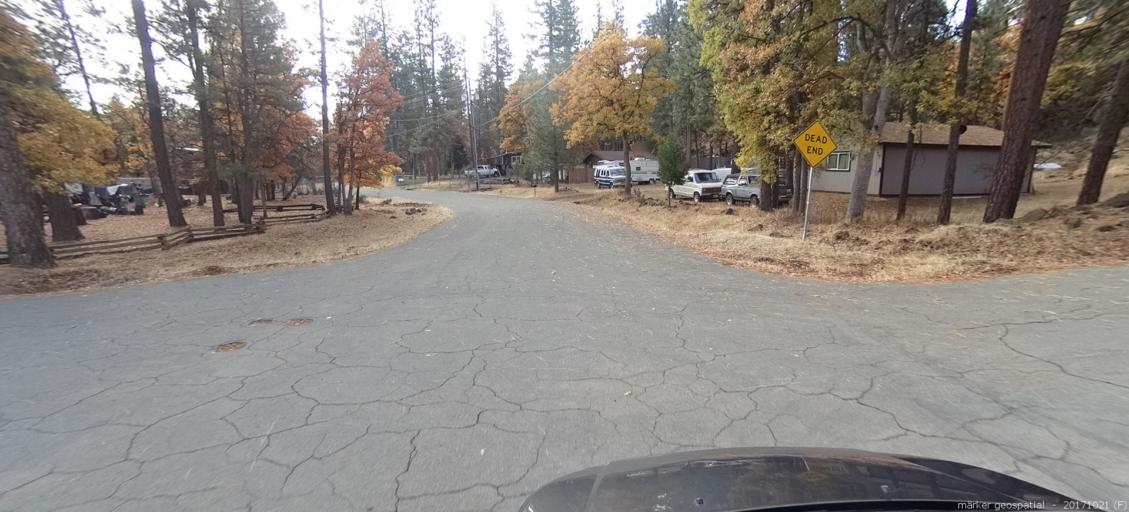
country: US
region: California
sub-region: Shasta County
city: Burney
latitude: 40.9150
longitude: -121.5585
